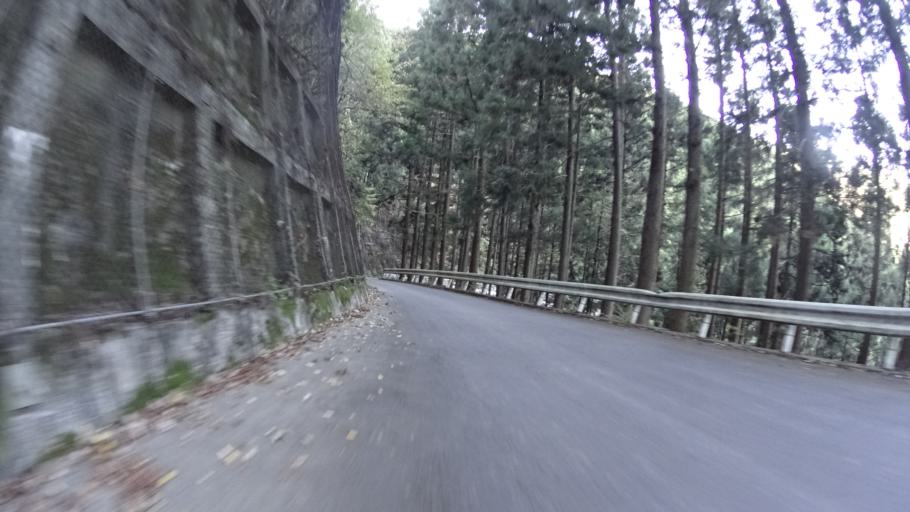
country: JP
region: Yamanashi
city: Uenohara
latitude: 35.6576
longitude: 139.1704
